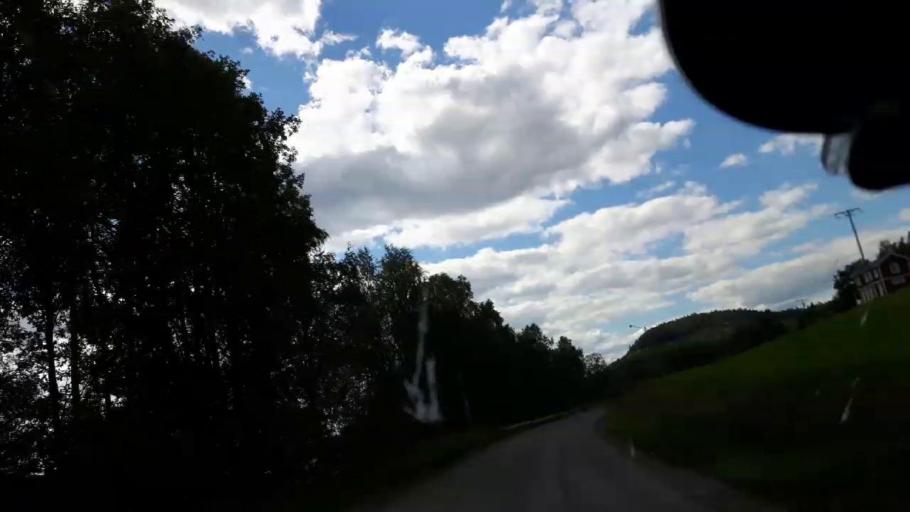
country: SE
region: Jaemtland
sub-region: Braecke Kommun
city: Braecke
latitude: 62.7174
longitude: 15.5943
